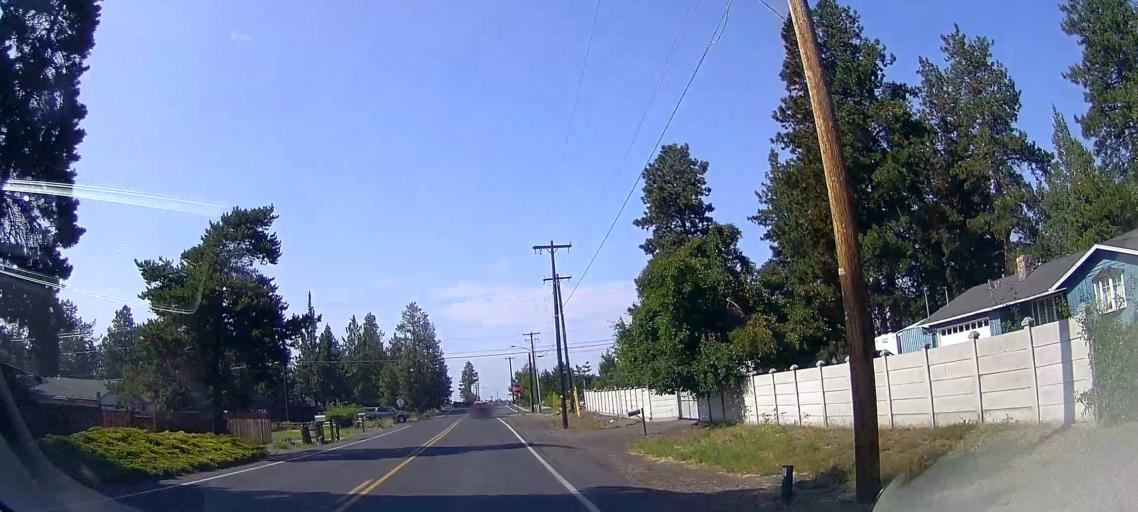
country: US
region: Oregon
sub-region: Deschutes County
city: Bend
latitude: 44.0508
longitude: -121.2686
